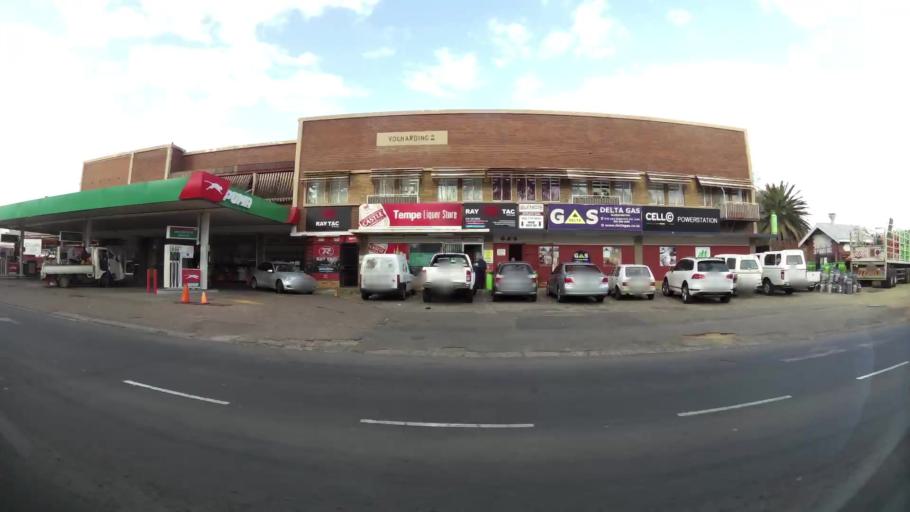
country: ZA
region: Orange Free State
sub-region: Mangaung Metropolitan Municipality
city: Bloemfontein
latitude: -29.0960
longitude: 26.2034
